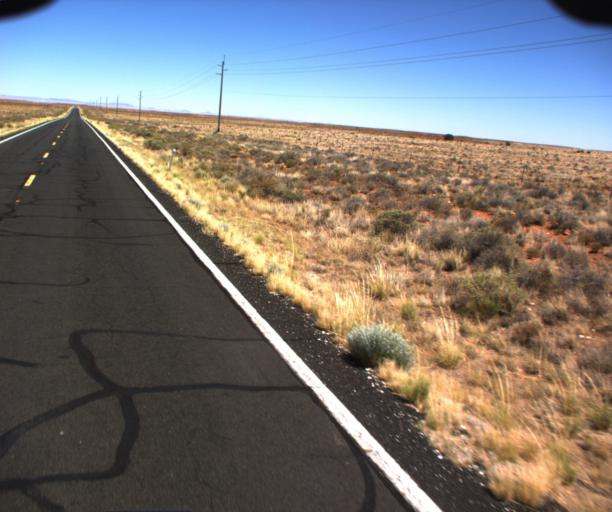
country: US
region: Arizona
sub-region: Coconino County
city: LeChee
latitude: 34.8942
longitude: -110.8631
